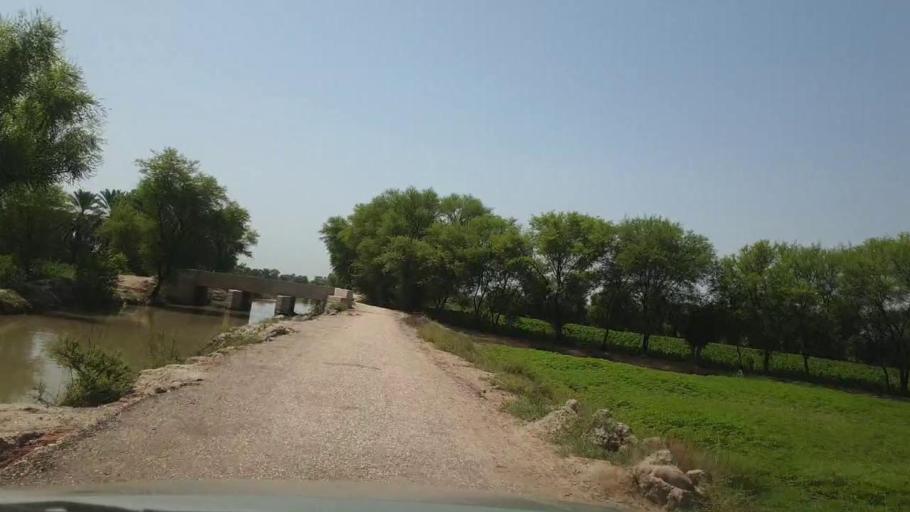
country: PK
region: Sindh
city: Rohri
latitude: 27.6540
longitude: 68.9831
